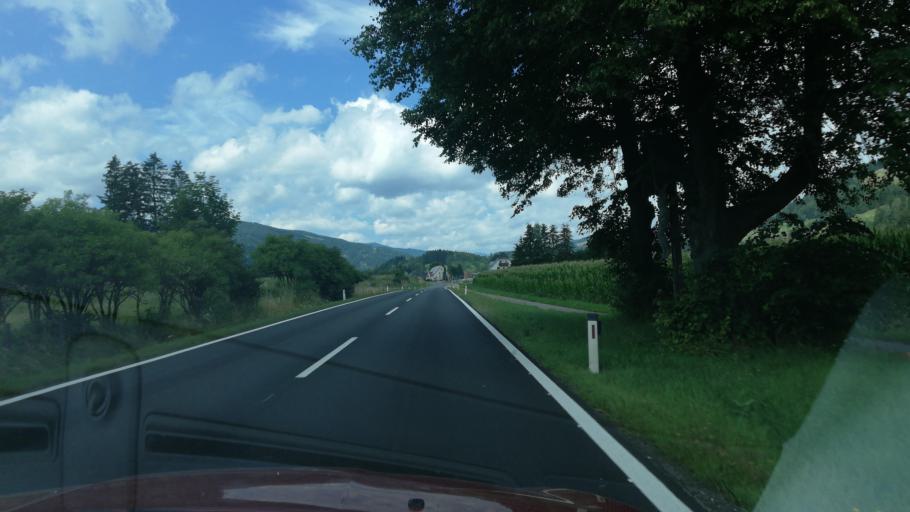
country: AT
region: Styria
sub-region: Politischer Bezirk Murtal
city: Oberzeiring
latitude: 47.2530
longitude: 14.5210
